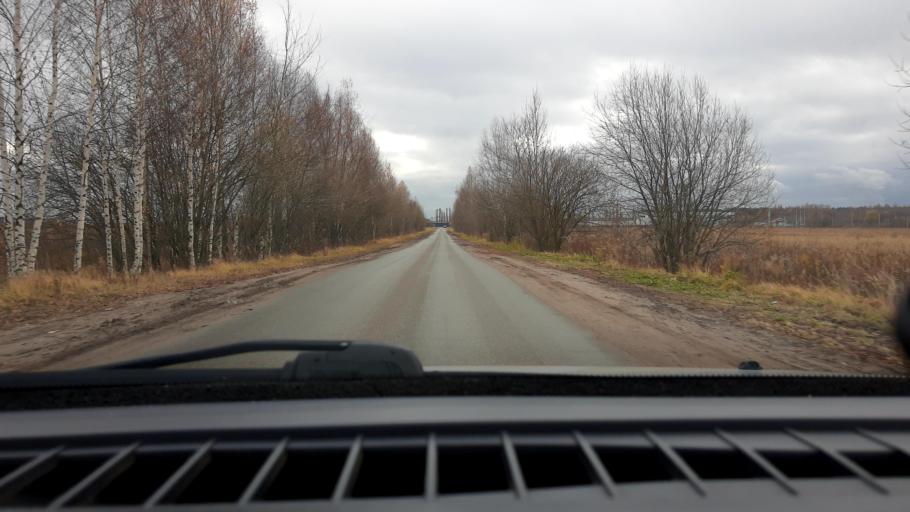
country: RU
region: Nizjnij Novgorod
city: Afonino
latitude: 56.1976
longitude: 44.1357
